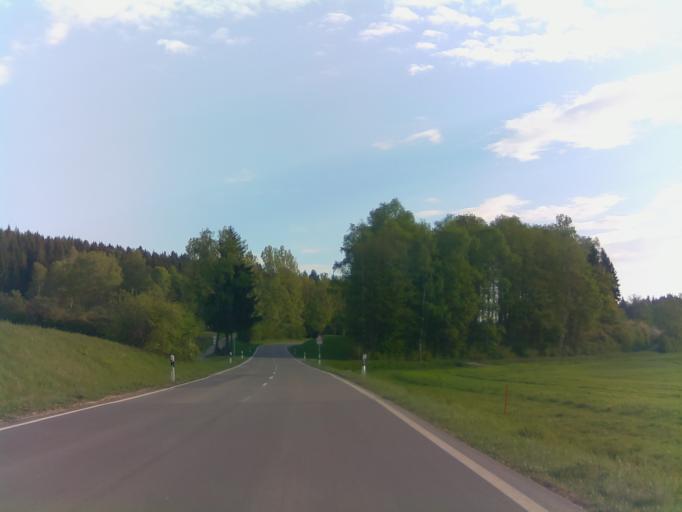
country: DE
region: Baden-Wuerttemberg
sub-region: Freiburg Region
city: Dietingen
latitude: 48.2132
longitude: 8.6541
